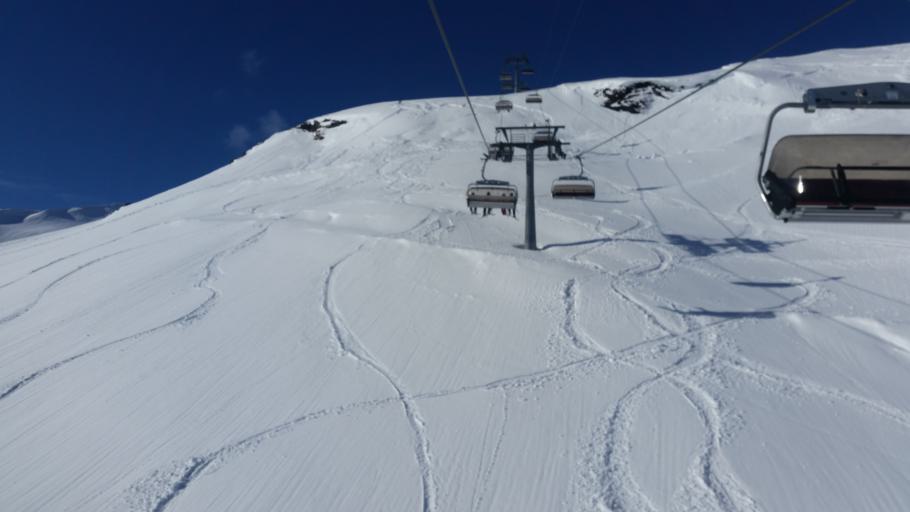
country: CH
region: Grisons
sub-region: Imboden District
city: Flims
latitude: 46.8650
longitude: 9.2231
